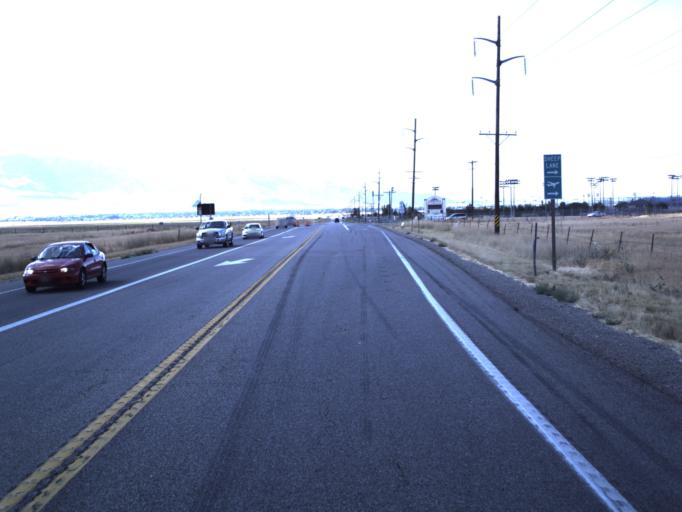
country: US
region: Utah
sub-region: Tooele County
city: Tooele
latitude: 40.5661
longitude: -112.3655
